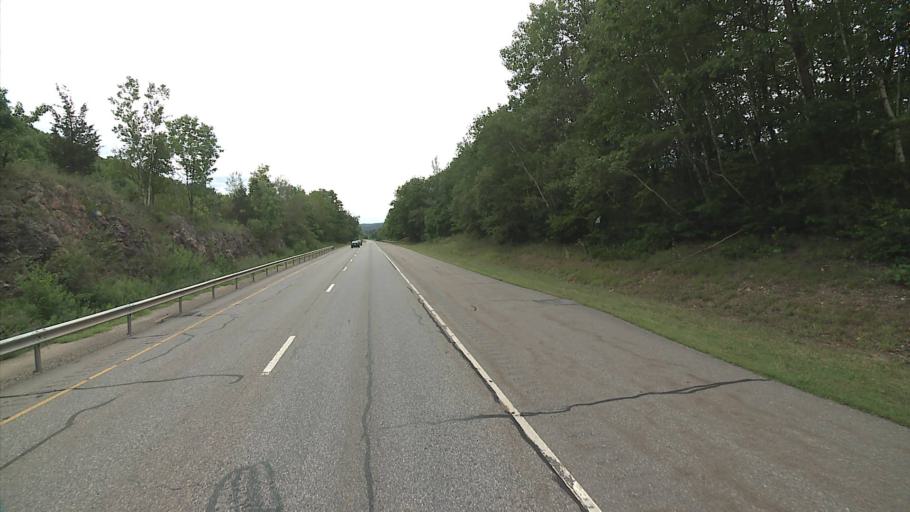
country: US
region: Connecticut
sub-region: Litchfield County
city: Torrington
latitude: 41.8354
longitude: -73.1018
